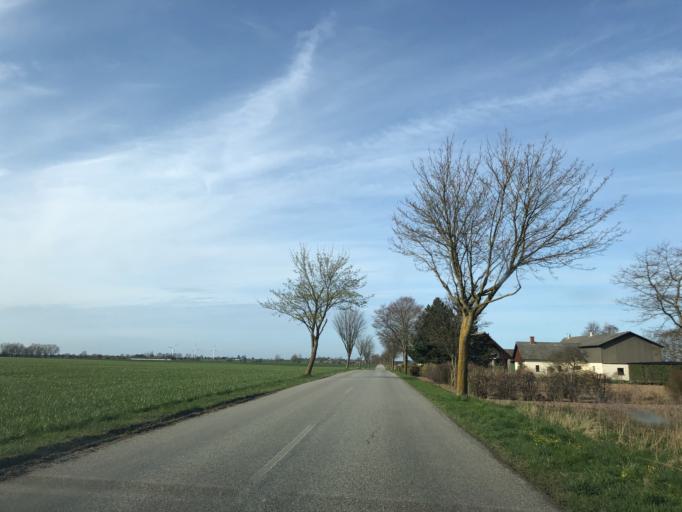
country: DK
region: Zealand
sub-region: Stevns Kommune
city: Store Heddinge
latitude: 55.3165
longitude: 12.4348
